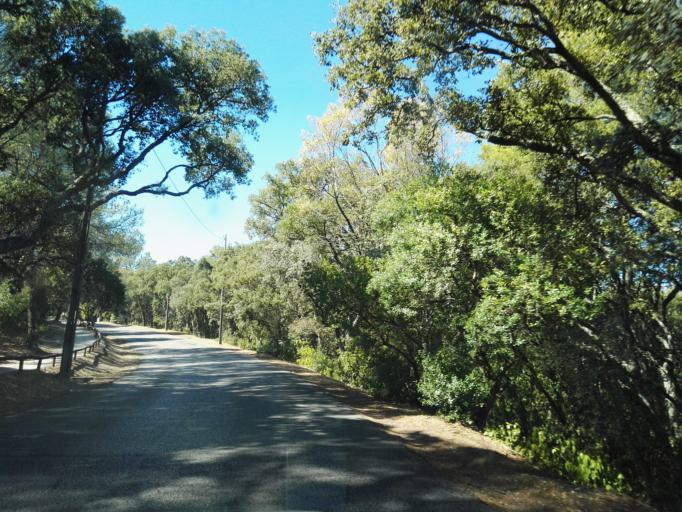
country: PT
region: Lisbon
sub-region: Odivelas
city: Pontinha
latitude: 38.7411
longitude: -9.1873
